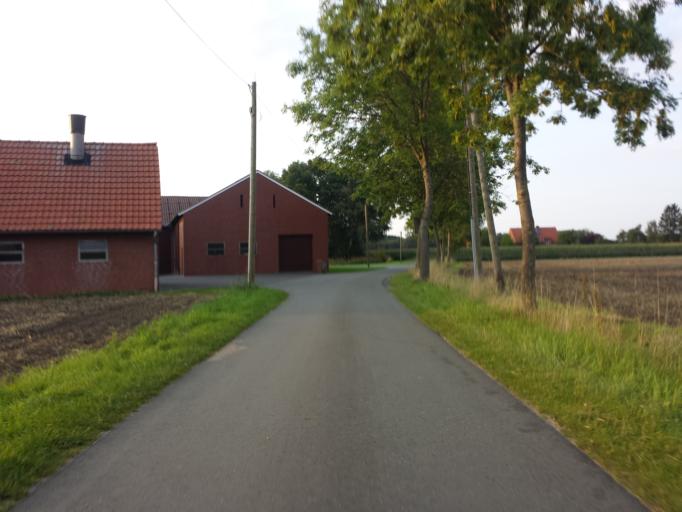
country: DE
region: North Rhine-Westphalia
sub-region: Regierungsbezirk Detmold
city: Guetersloh
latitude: 51.9364
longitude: 8.3164
